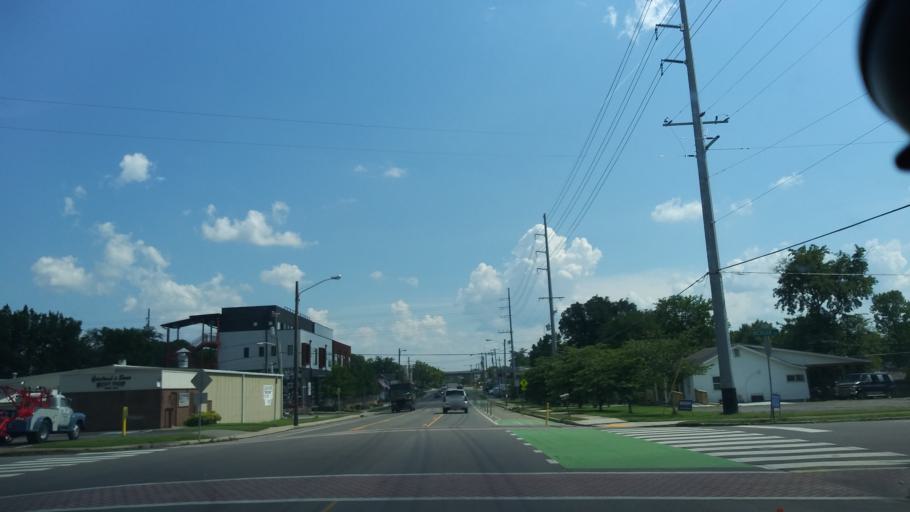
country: US
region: Tennessee
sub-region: Davidson County
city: Belle Meade
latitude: 36.1589
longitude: -86.8490
